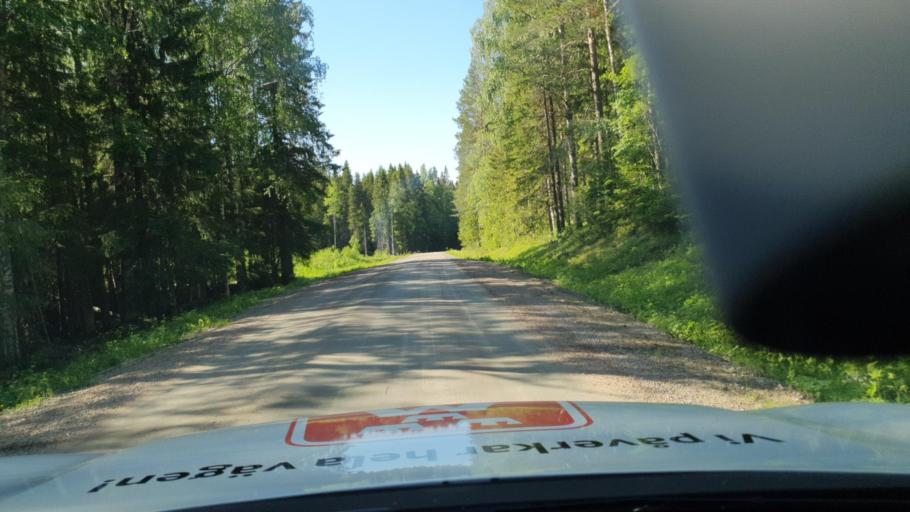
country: SE
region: Vaesterbotten
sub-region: Vannas Kommun
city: Vaennaes
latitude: 63.8439
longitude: 19.6245
